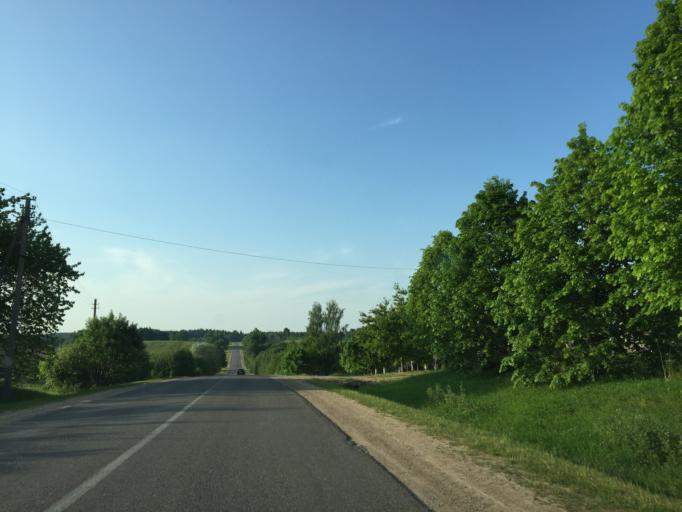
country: LT
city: Plateliai
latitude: 56.0496
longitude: 21.8189
